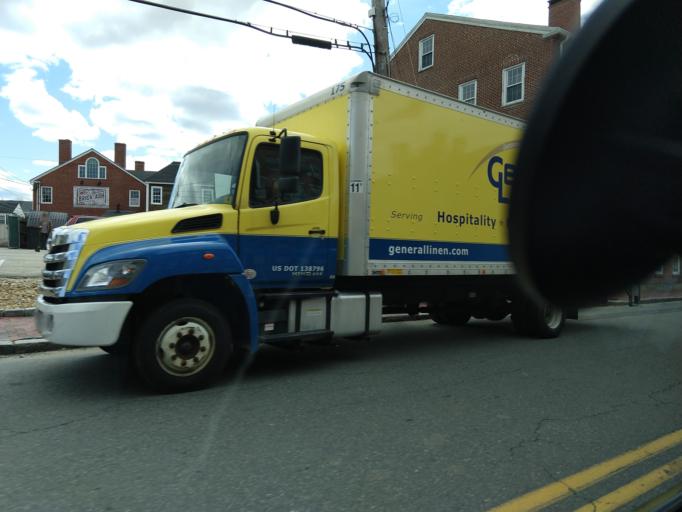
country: US
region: Massachusetts
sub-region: Essex County
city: Newburyport
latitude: 42.8117
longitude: -70.8678
